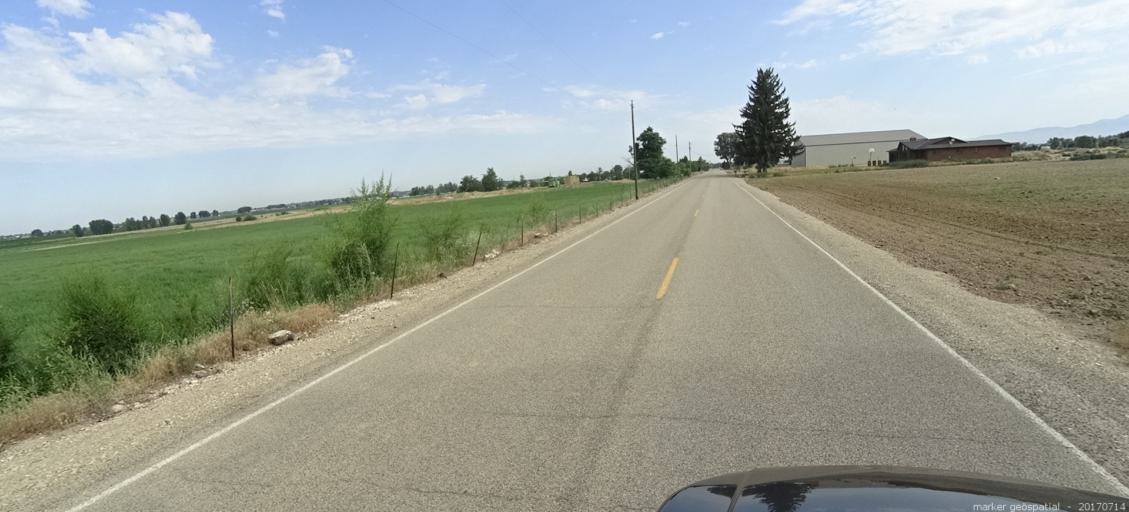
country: US
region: Idaho
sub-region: Ada County
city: Kuna
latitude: 43.4919
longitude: -116.3543
